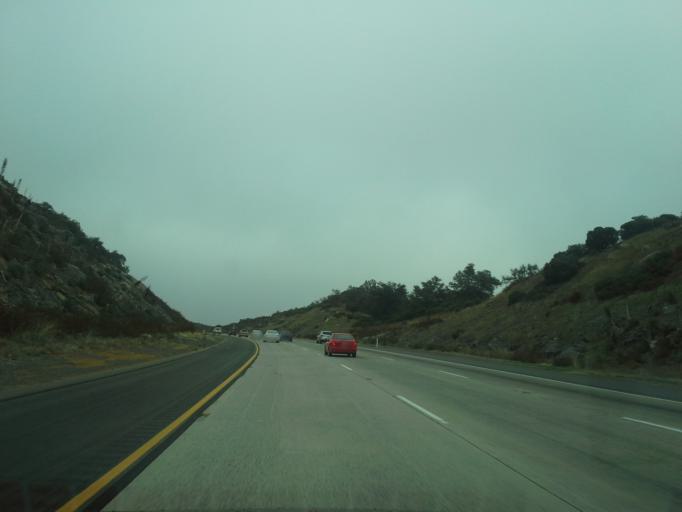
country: US
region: California
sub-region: San Diego County
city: Descanso
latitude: 32.8188
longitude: -116.5849
